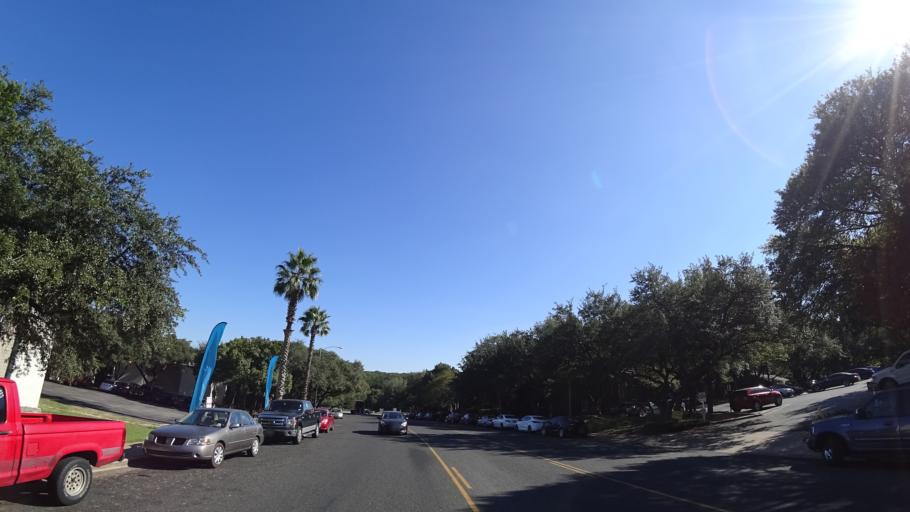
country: US
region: Texas
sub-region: Travis County
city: Rollingwood
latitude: 30.2588
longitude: -97.7884
